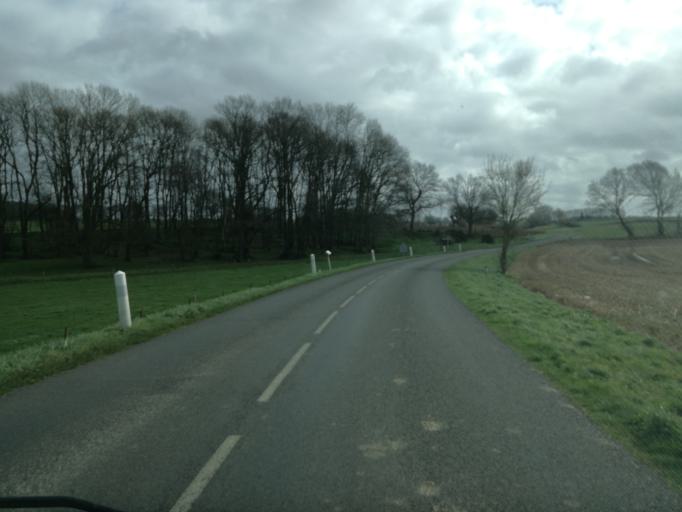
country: FR
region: Haute-Normandie
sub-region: Departement de la Seine-Maritime
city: Fauville-en-Caux
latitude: 49.6568
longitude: 0.5739
